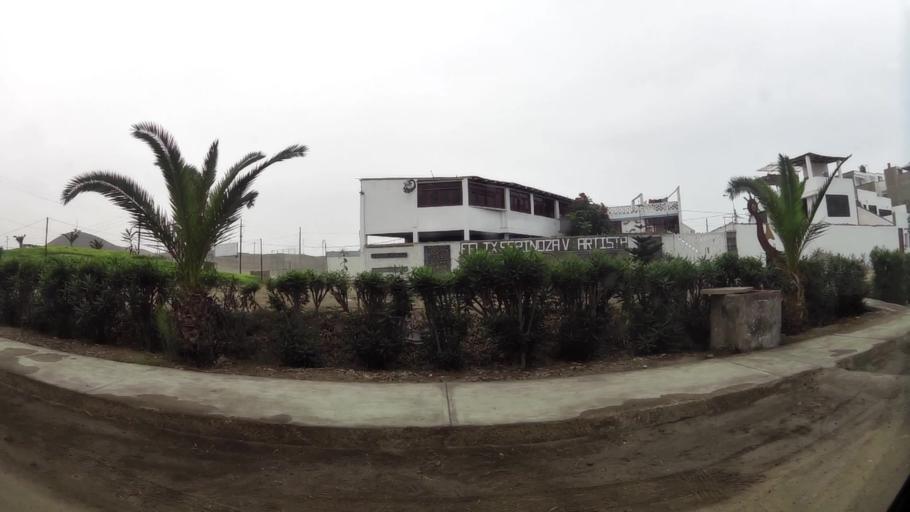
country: PE
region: Lima
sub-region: Lima
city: Punta Hermosa
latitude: -12.3351
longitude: -76.8208
